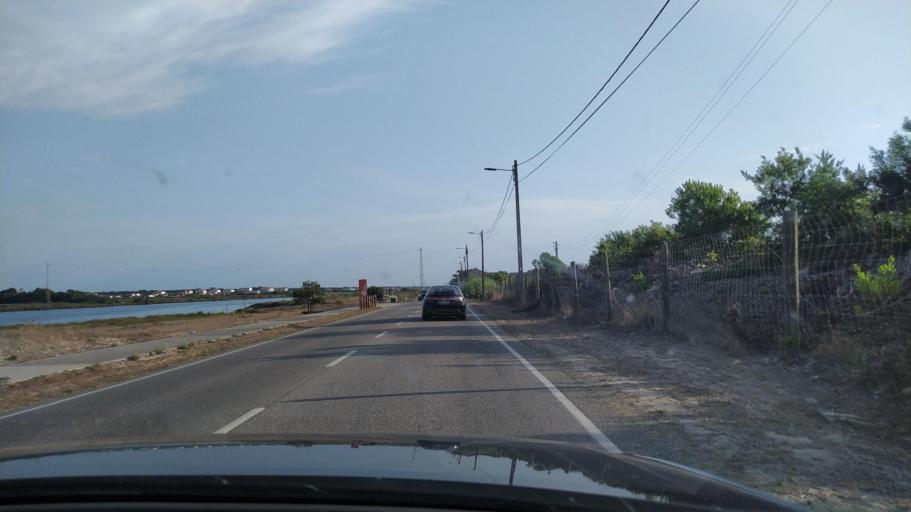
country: PT
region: Aveiro
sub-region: Ilhavo
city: Gafanha da Encarnacao
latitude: 40.5737
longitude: -8.7563
